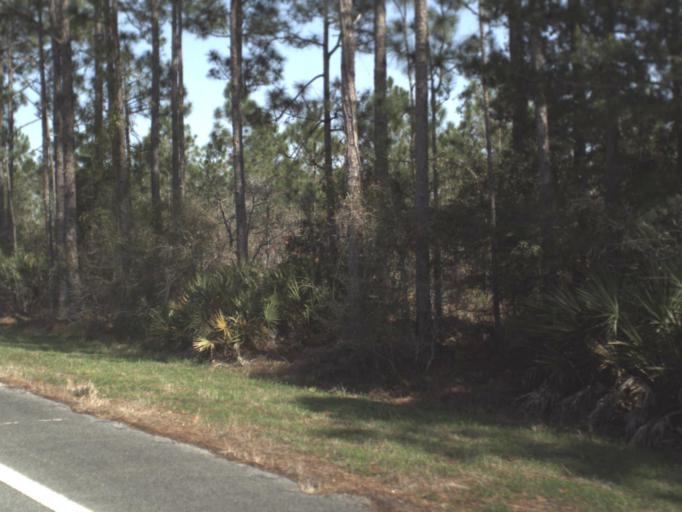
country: US
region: Florida
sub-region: Franklin County
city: Carrabelle
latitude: 29.9348
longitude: -84.5070
